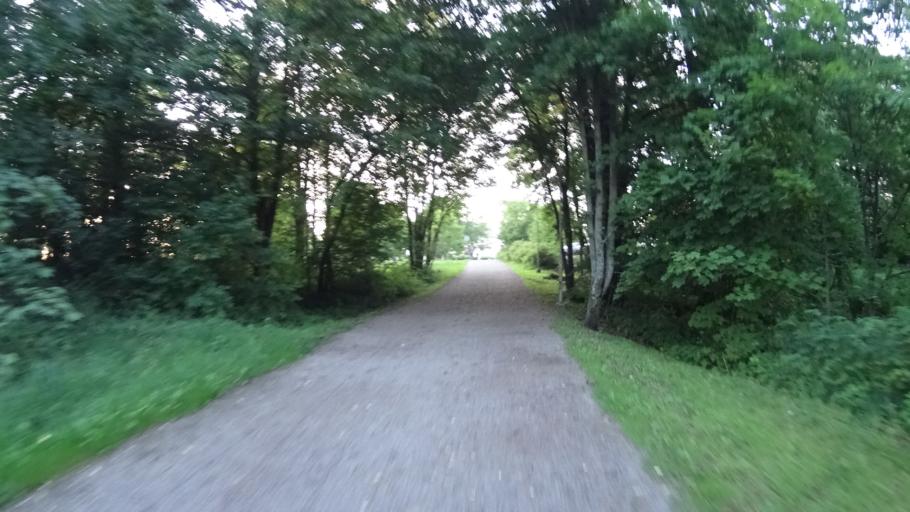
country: FI
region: Uusimaa
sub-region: Helsinki
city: Teekkarikylae
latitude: 60.2108
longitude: 24.8610
